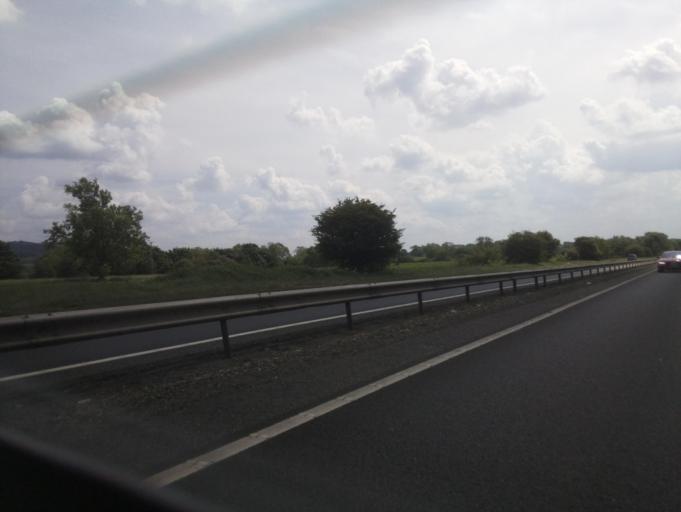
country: GB
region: England
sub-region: North Yorkshire
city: Thirsk
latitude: 54.2954
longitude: -1.3371
